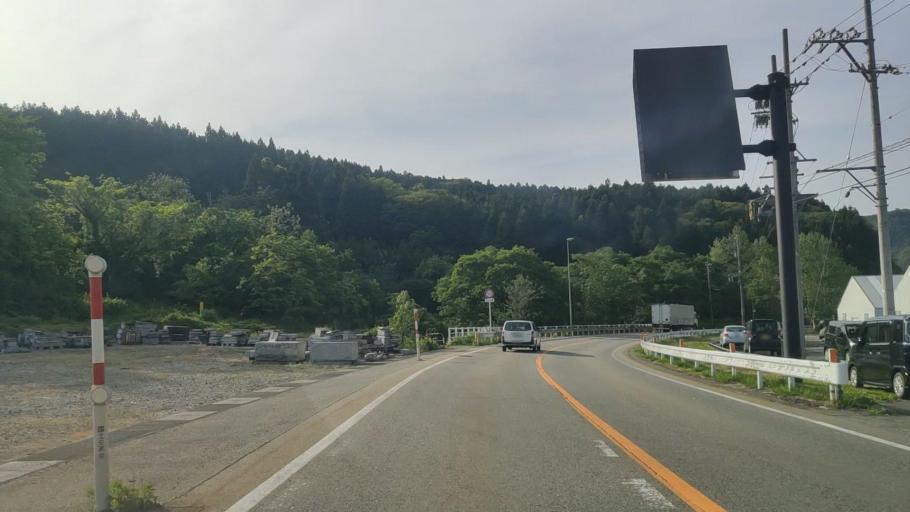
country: JP
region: Toyama
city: Yatsuomachi-higashikumisaka
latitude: 36.5393
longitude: 137.2297
